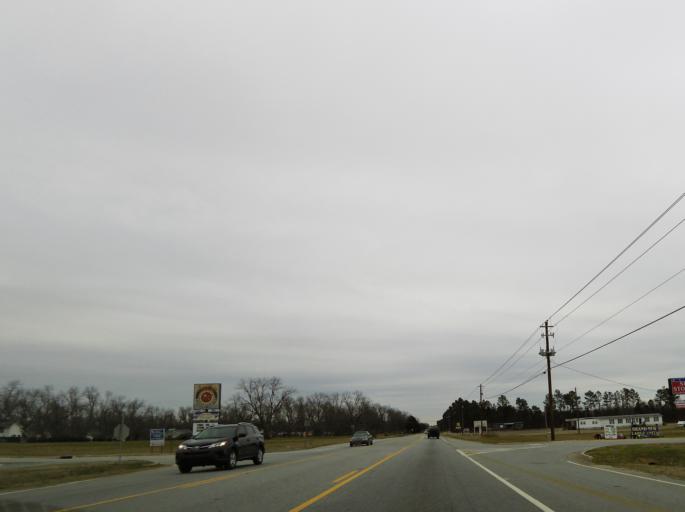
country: US
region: Georgia
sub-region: Peach County
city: Byron
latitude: 32.6631
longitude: -83.7391
